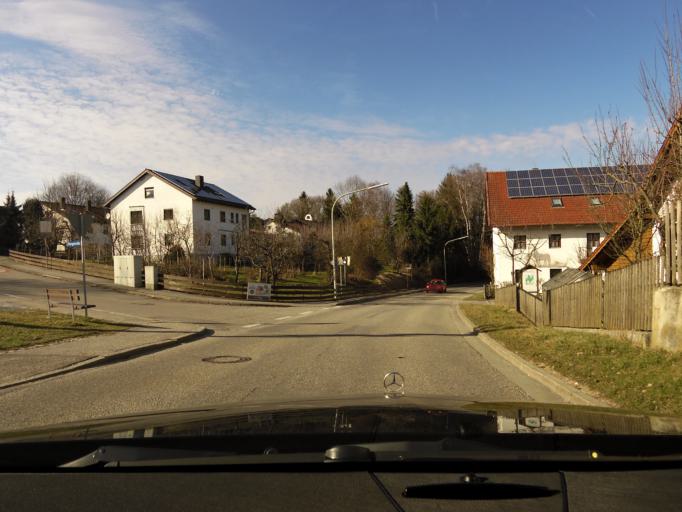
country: DE
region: Bavaria
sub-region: Lower Bavaria
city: Tiefenbach
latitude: 48.5031
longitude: 12.0995
